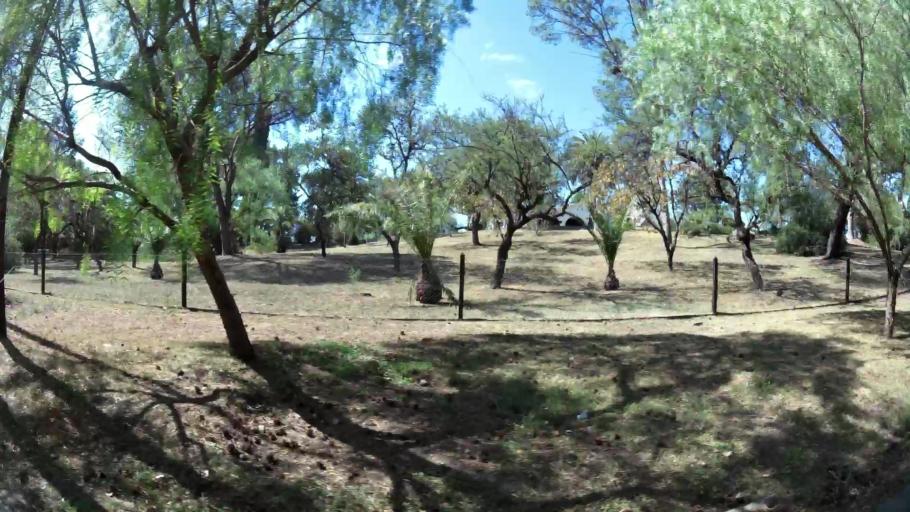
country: AR
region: Cordoba
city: Mendiolaza
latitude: -31.2744
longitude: -64.2935
